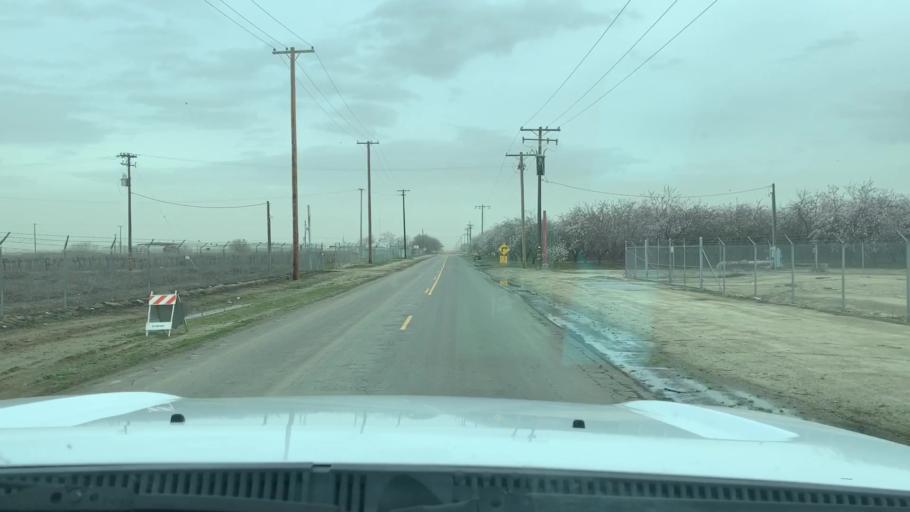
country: US
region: California
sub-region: Kern County
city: Shafter
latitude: 35.5293
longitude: -119.2630
